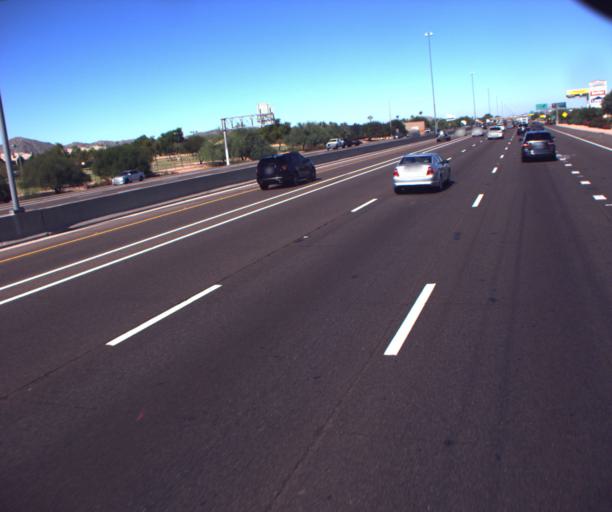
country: US
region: Arizona
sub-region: Maricopa County
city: Guadalupe
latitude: 33.3244
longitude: -111.9721
